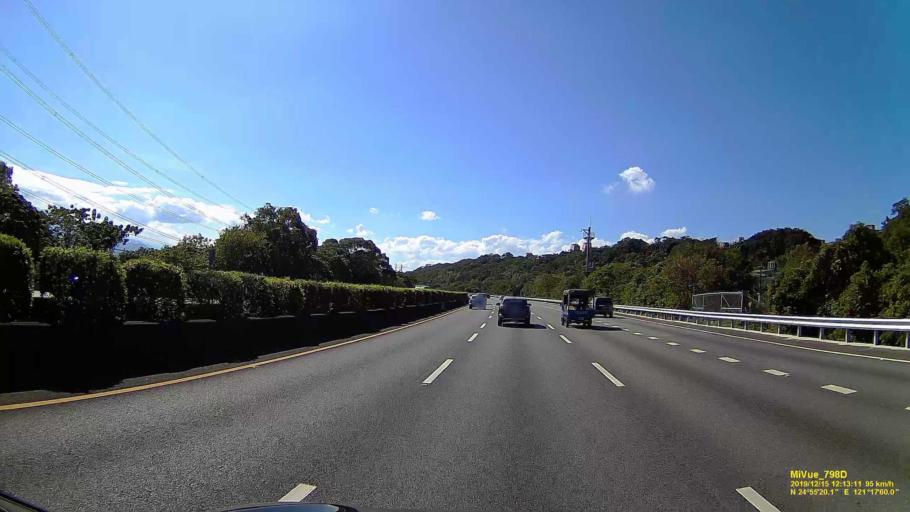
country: TW
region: Taiwan
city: Daxi
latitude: 24.9219
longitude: 121.2998
